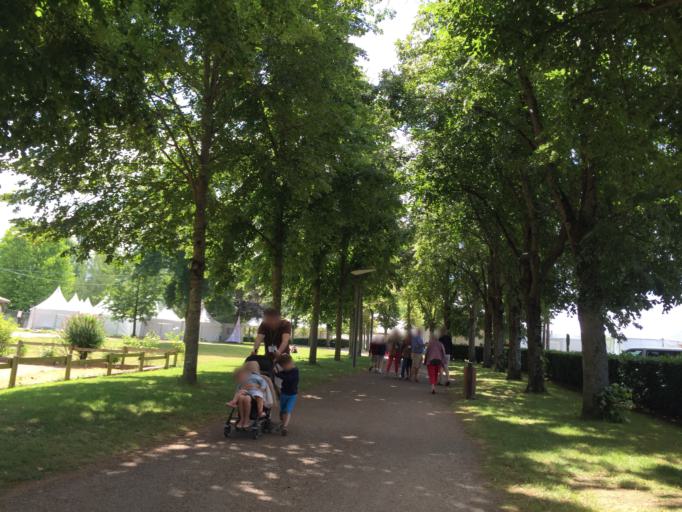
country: FR
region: Bourgogne
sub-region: Departement de Saone-et-Loire
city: Paray-le-Monial
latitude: 46.4477
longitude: 4.1208
